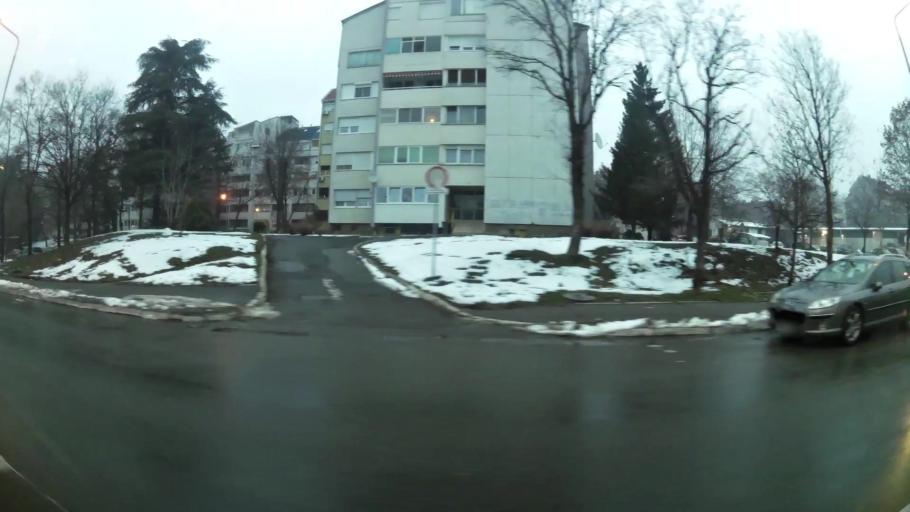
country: RS
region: Central Serbia
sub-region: Belgrade
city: Vozdovac
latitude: 44.7692
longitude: 20.4974
